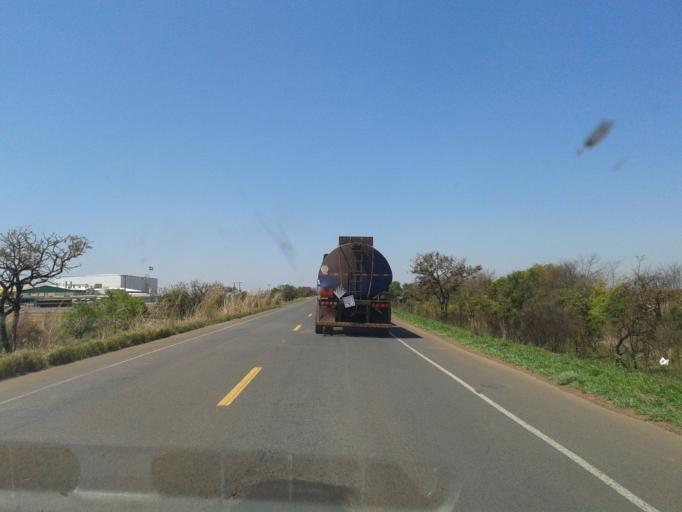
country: BR
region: Minas Gerais
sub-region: Araxa
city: Araxa
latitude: -19.3109
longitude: -47.3906
